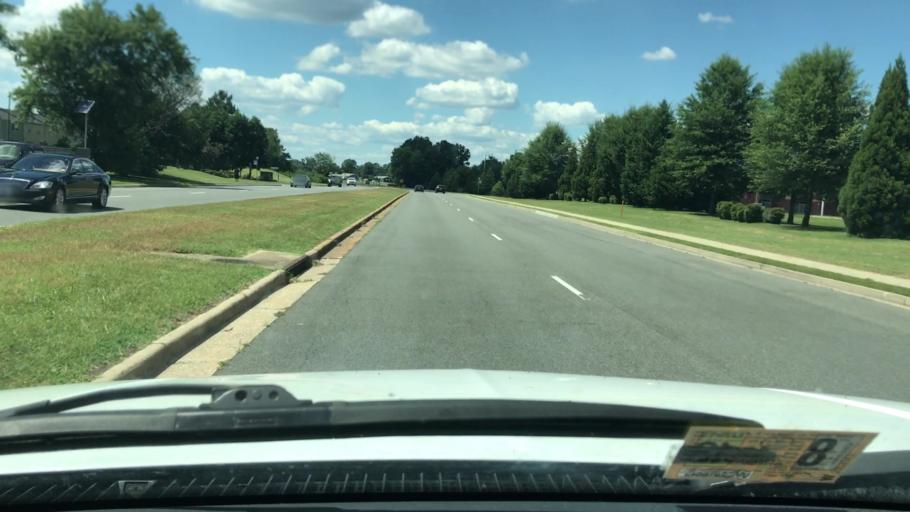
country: US
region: Virginia
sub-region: Henrico County
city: East Highland Park
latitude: 37.5685
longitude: -77.3798
